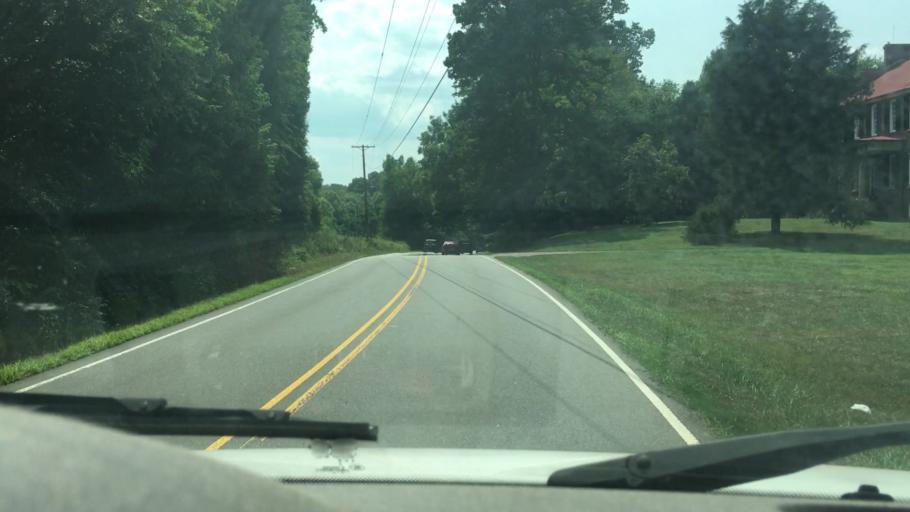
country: US
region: North Carolina
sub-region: Mecklenburg County
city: Huntersville
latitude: 35.4069
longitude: -80.8869
